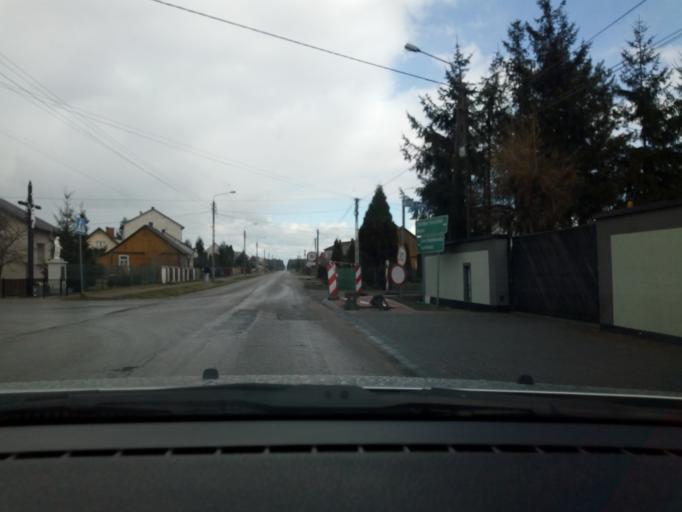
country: PL
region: Swietokrzyskie
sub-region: Powiat skarzyski
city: Skarzysko Koscielne
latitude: 51.1560
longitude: 20.9100
